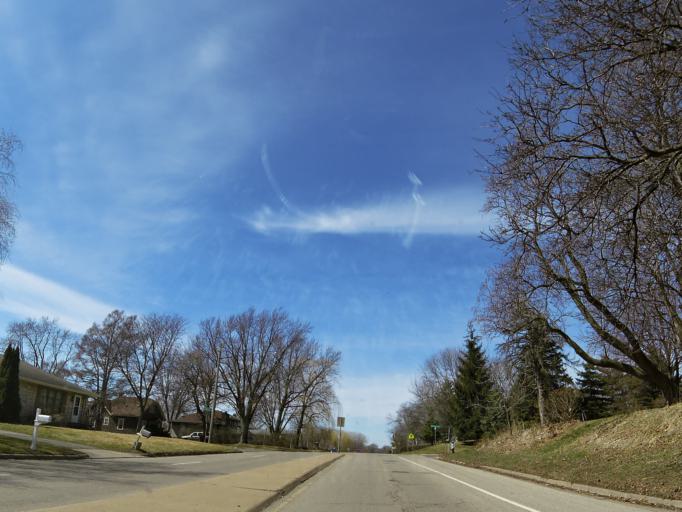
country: US
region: Minnesota
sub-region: Ramsey County
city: North Saint Paul
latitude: 44.9921
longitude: -93.0270
